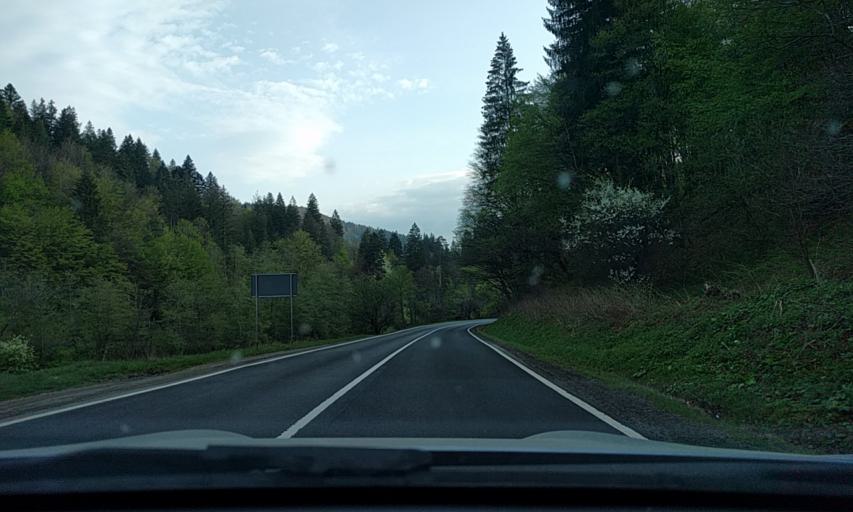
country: RO
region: Covasna
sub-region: Comuna Bretcu
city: Bretcu
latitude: 46.0785
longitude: 26.3956
